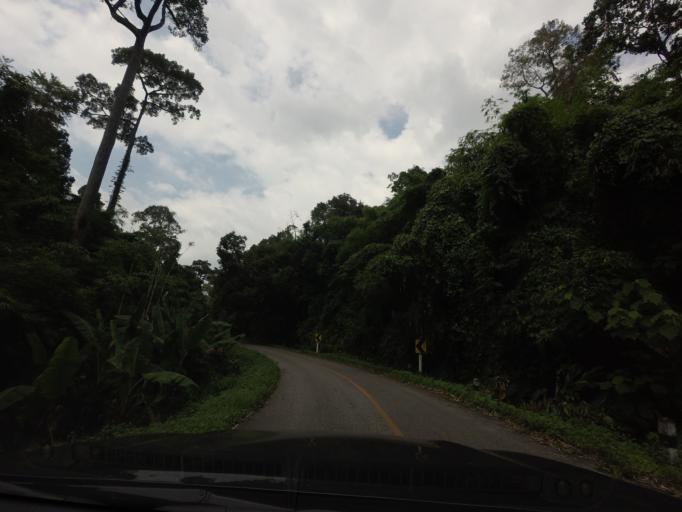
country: TH
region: Loei
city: Na Haeo
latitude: 17.7164
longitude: 100.9474
